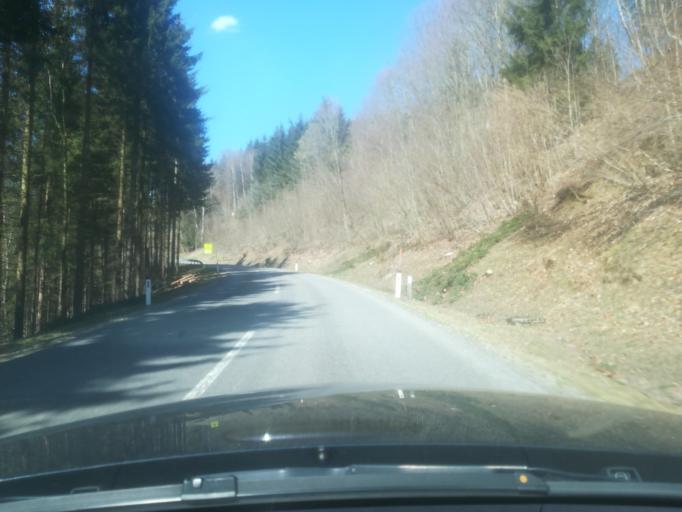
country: AT
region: Lower Austria
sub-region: Politischer Bezirk Zwettl
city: Langschlag
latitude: 48.4640
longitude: 14.7975
